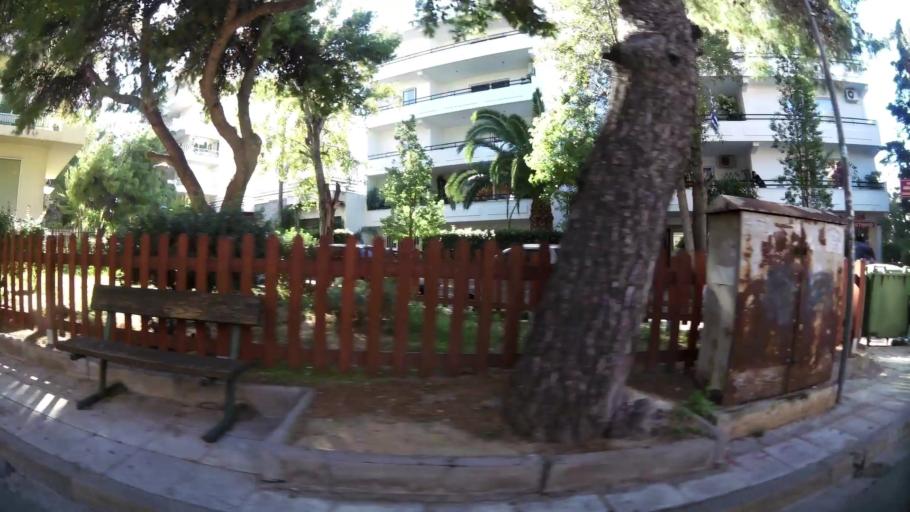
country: GR
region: Attica
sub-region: Nomarchia Athinas
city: Metamorfosi
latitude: 38.0619
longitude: 23.7658
